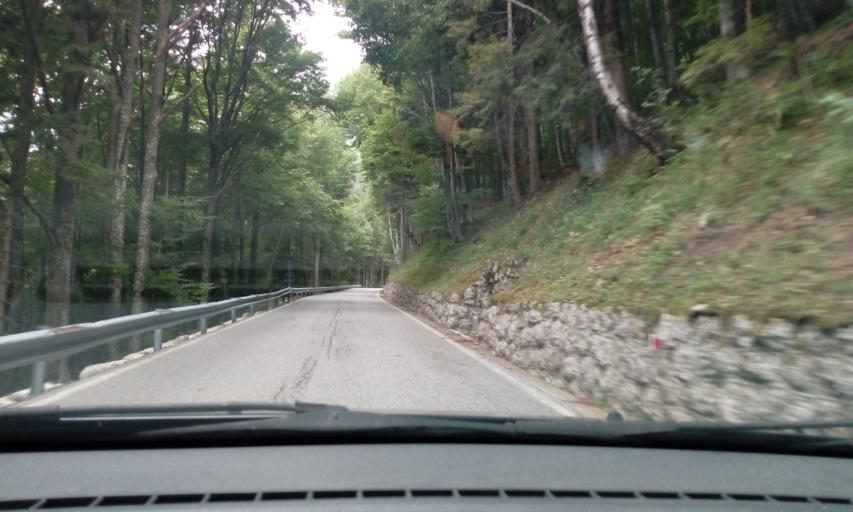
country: SI
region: Bovec
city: Bovec
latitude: 46.3907
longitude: 13.4647
